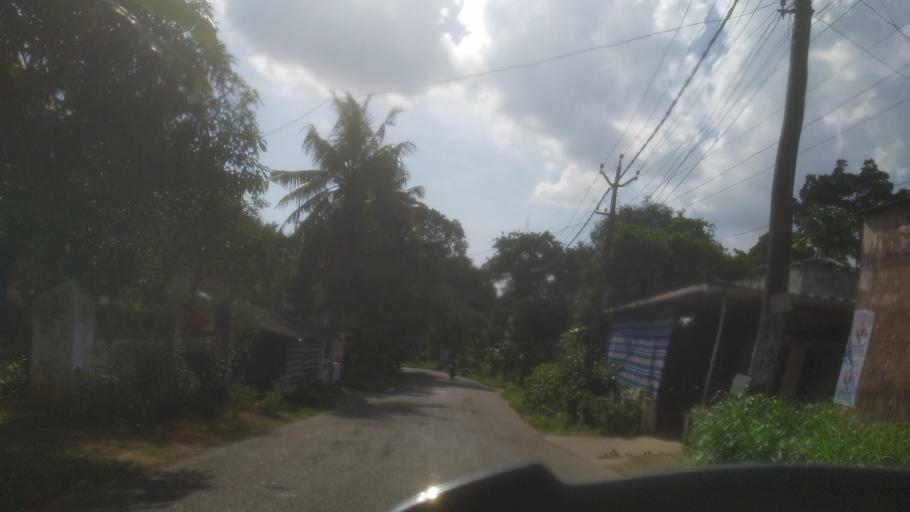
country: IN
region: Kerala
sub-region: Ernakulam
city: Muvattupula
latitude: 9.9982
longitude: 76.6199
